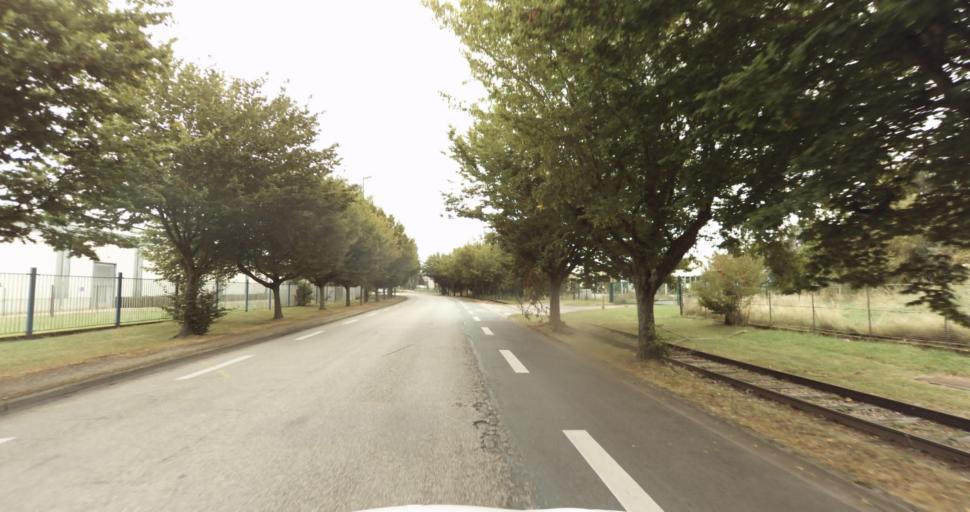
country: FR
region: Haute-Normandie
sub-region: Departement de l'Eure
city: Evreux
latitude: 49.0193
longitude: 1.1758
